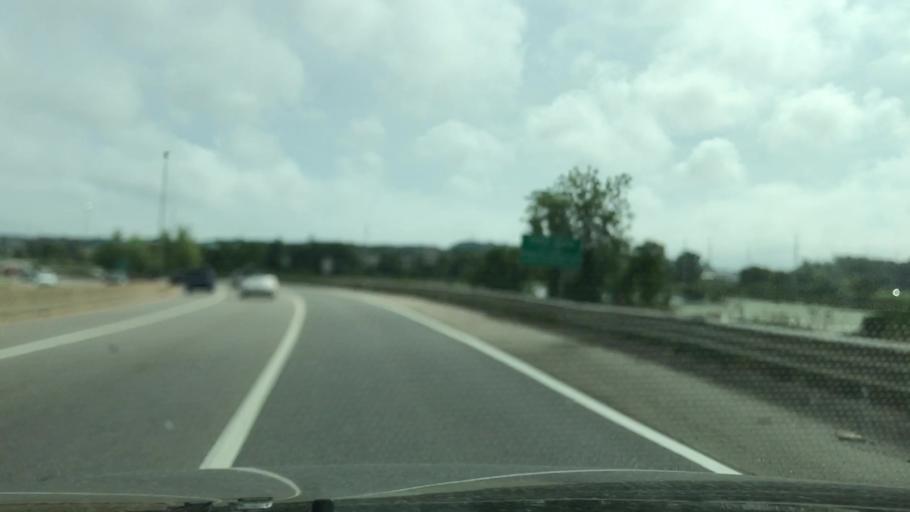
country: US
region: Michigan
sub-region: Ottawa County
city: Ferrysburg
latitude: 43.0743
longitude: -86.2188
